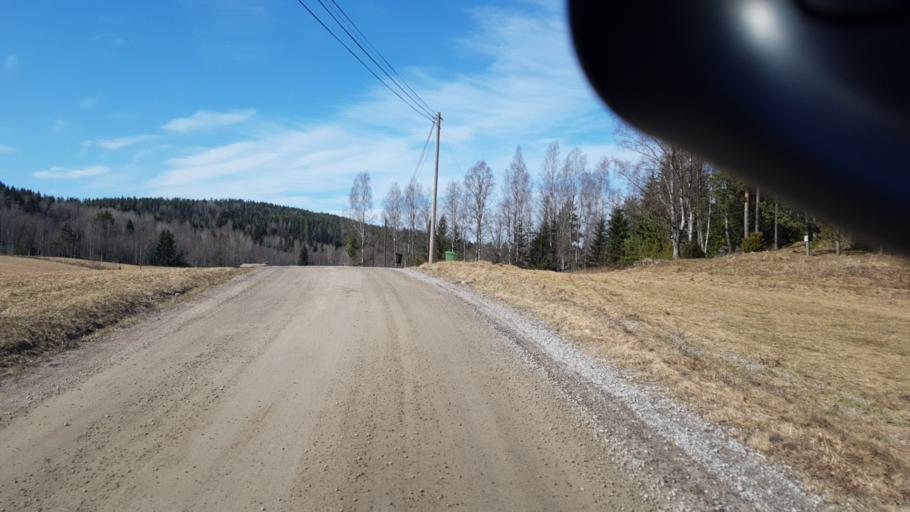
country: SE
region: Vaermland
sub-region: Sunne Kommun
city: Sunne
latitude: 59.6886
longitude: 12.8913
